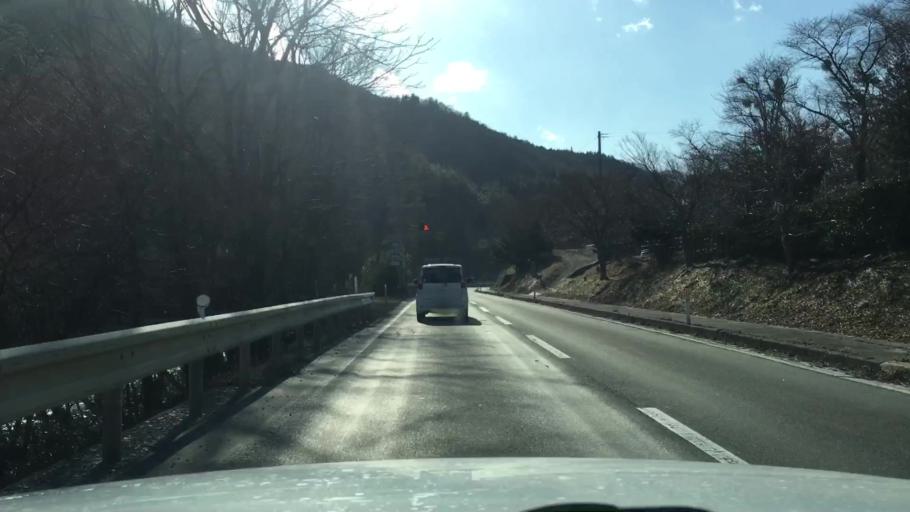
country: JP
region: Iwate
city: Miyako
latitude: 39.6031
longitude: 141.6940
